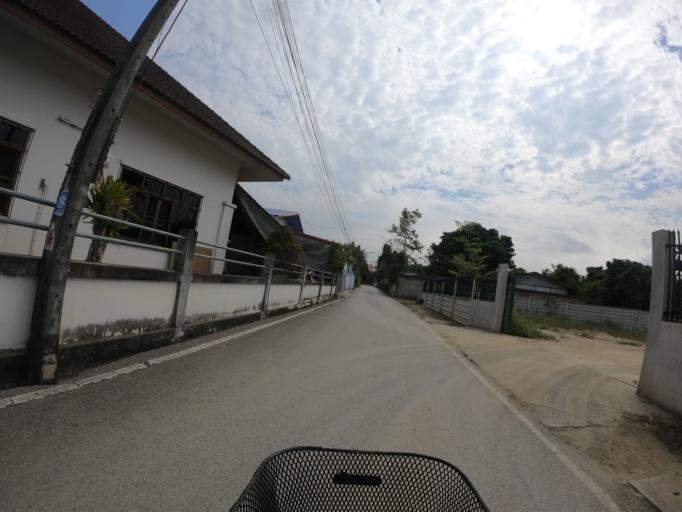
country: TH
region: Chiang Mai
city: Saraphi
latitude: 18.7053
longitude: 99.0379
